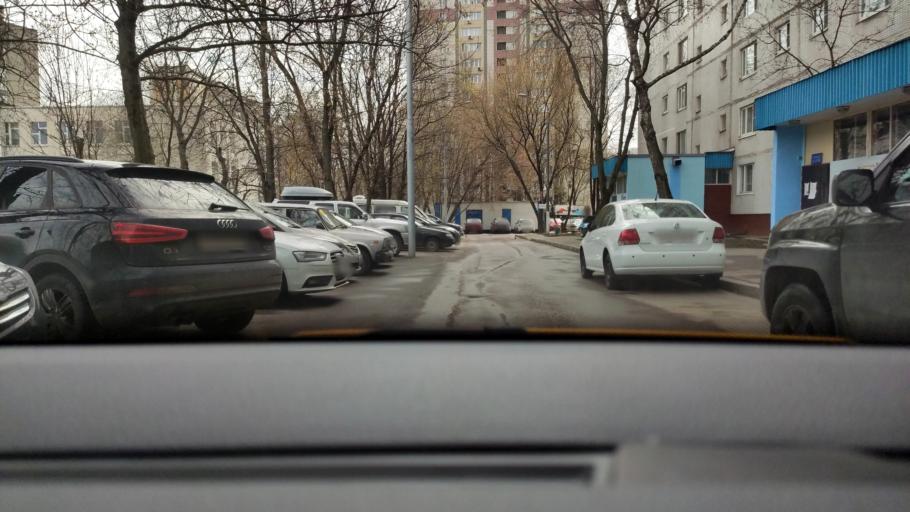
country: RU
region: Moscow
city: Otradnoye
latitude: 55.8666
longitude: 37.5999
